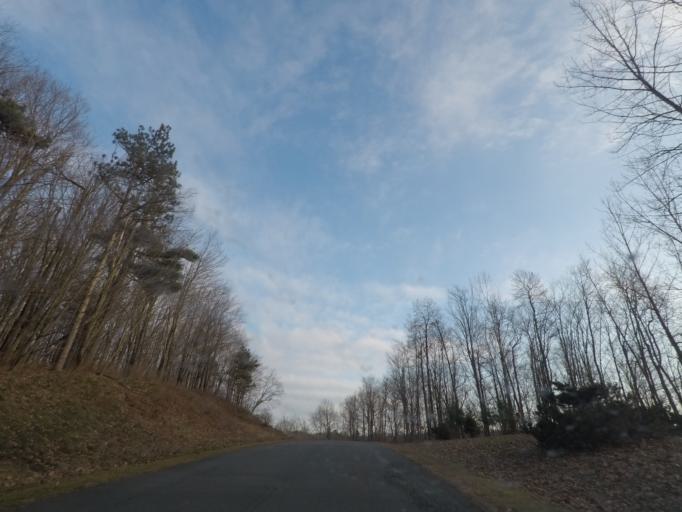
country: US
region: New York
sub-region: Rensselaer County
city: Wynantskill
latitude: 42.7224
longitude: -73.6430
